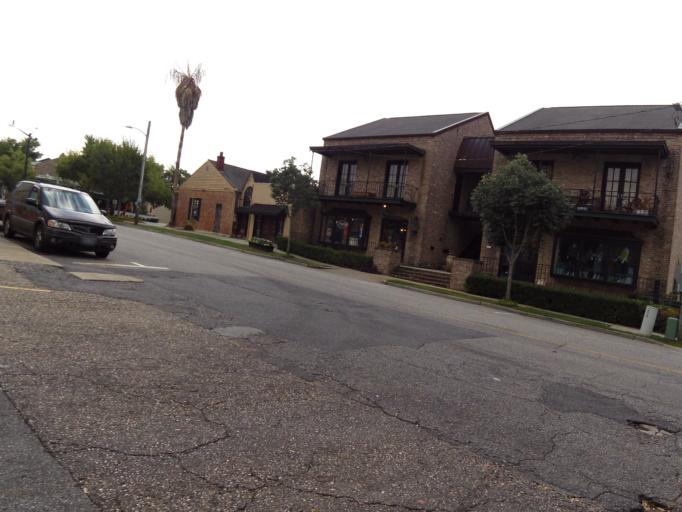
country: US
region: Alabama
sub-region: Baldwin County
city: Fairhope
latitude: 30.5237
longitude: -87.9047
